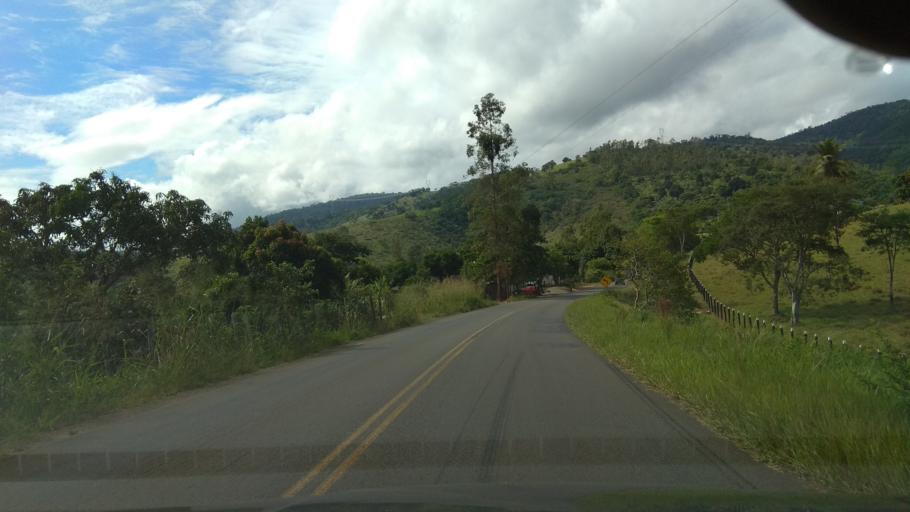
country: BR
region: Bahia
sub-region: Ubaira
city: Ubaira
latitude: -13.2710
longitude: -39.6368
